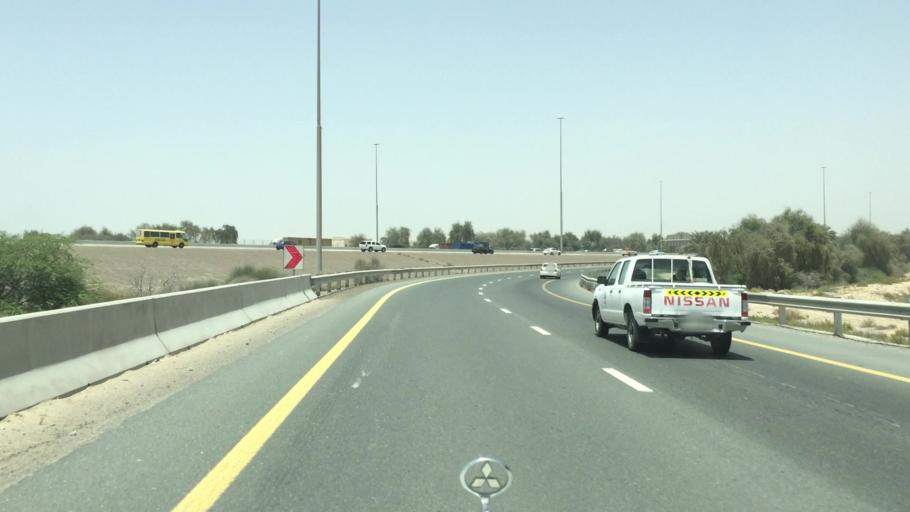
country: AE
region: Dubai
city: Dubai
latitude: 25.1201
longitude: 55.3674
